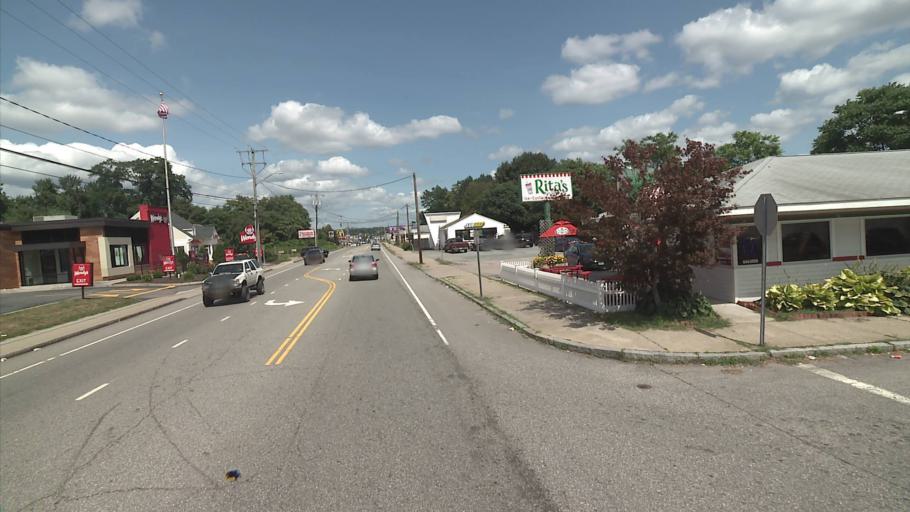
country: US
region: Connecticut
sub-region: New London County
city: New London
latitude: 41.3585
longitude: -72.1159
